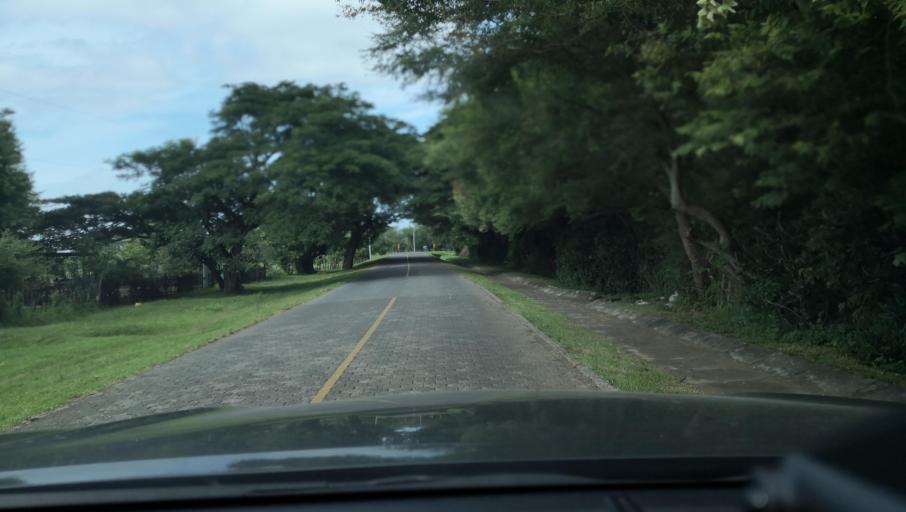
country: NI
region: Masaya
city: Tisma
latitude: 12.1034
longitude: -85.8905
